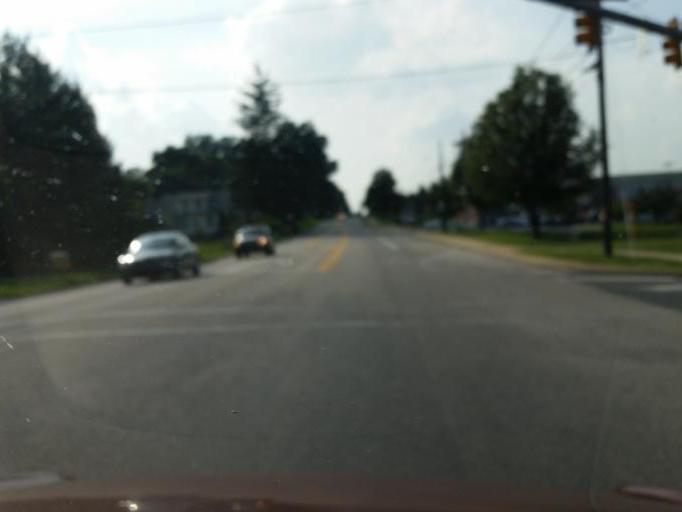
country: US
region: Pennsylvania
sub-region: Dauphin County
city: Hershey
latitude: 40.2675
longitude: -76.6478
